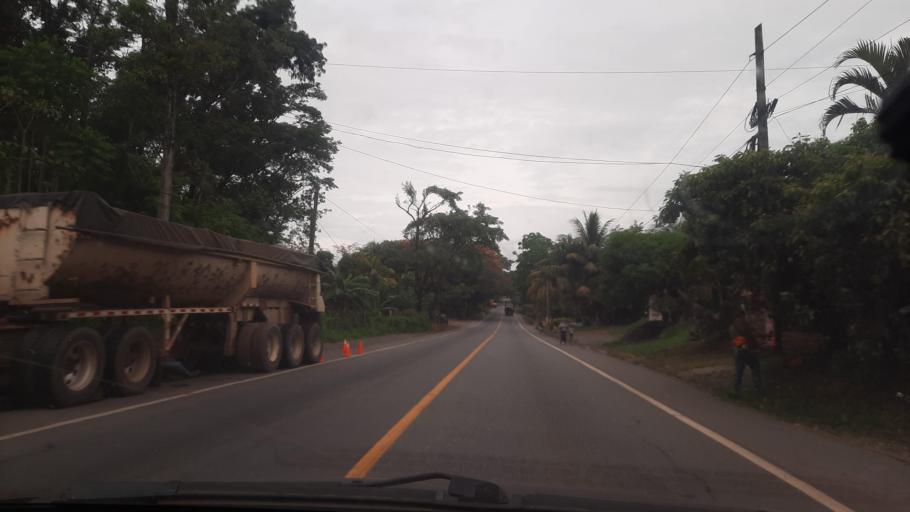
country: GT
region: Izabal
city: Morales
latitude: 15.4362
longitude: -88.9585
